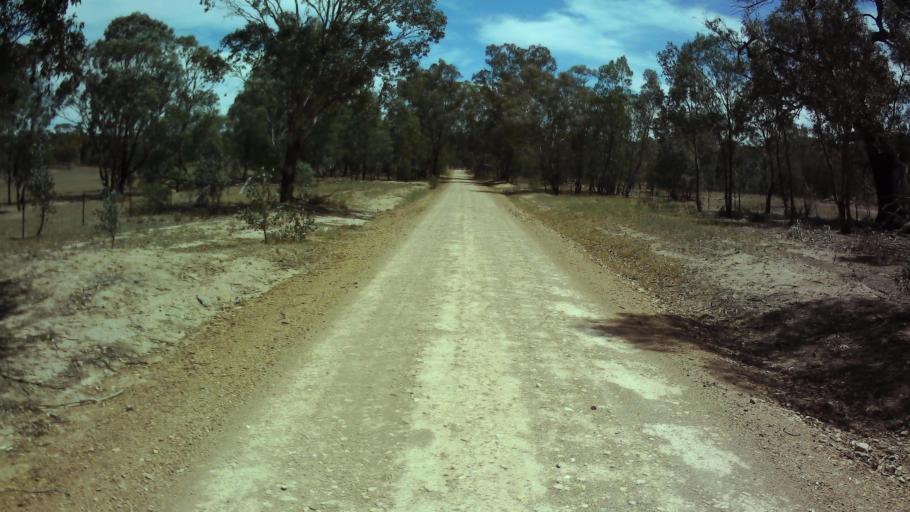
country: AU
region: New South Wales
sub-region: Weddin
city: Grenfell
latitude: -33.7474
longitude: 148.1942
